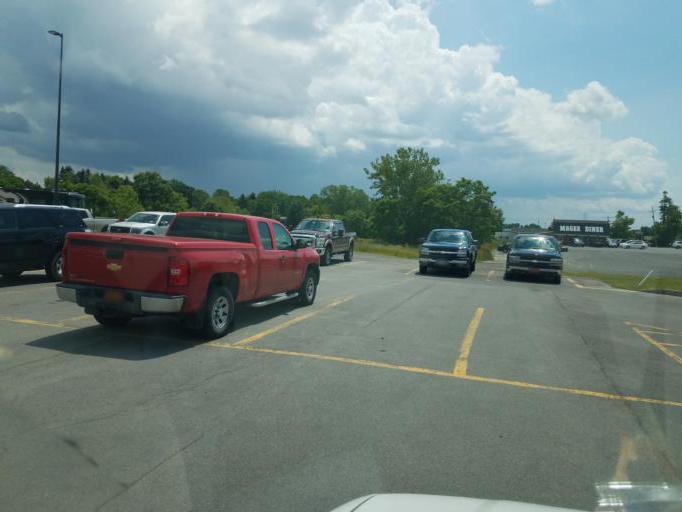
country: US
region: New York
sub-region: Seneca County
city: Waterloo
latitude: 42.9637
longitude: -76.8460
